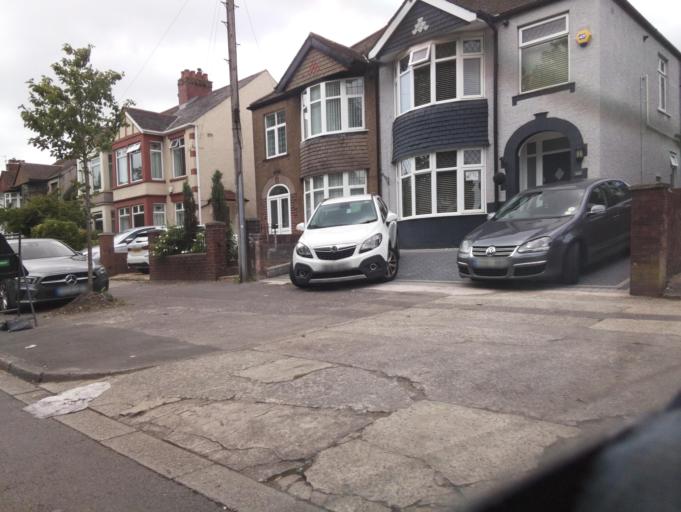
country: GB
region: Wales
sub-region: Cardiff
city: Radyr
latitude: 51.4809
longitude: -3.2375
